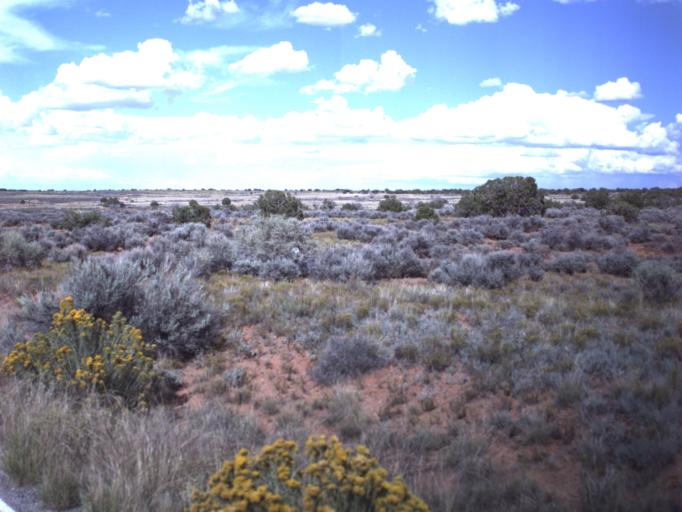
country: US
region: Utah
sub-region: Grand County
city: Moab
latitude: 38.5055
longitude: -109.7303
